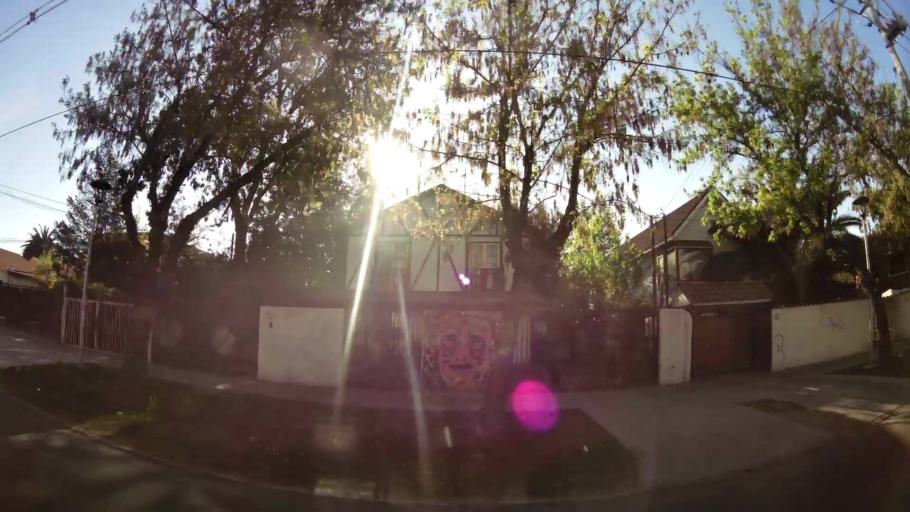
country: CL
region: Santiago Metropolitan
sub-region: Provincia de Santiago
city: Villa Presidente Frei, Nunoa, Santiago, Chile
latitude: -33.4520
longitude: -70.5653
